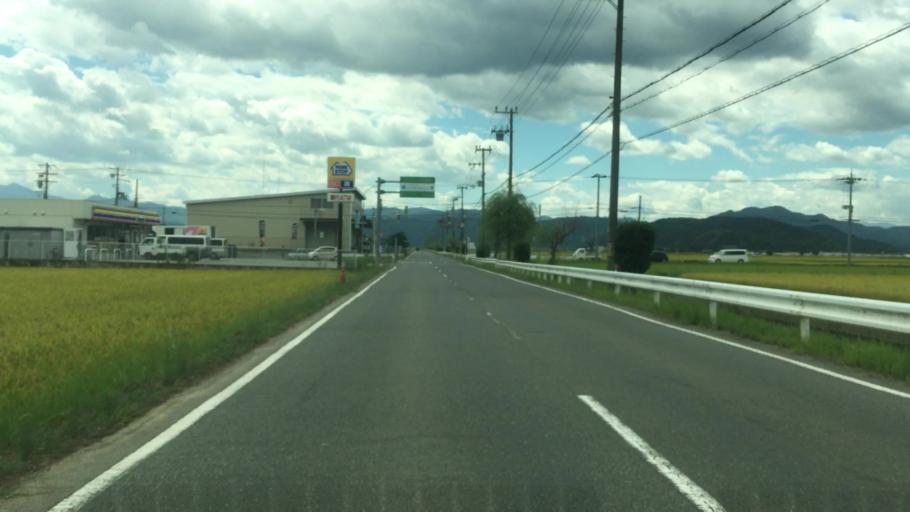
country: JP
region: Hyogo
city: Toyooka
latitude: 35.5257
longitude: 134.8398
